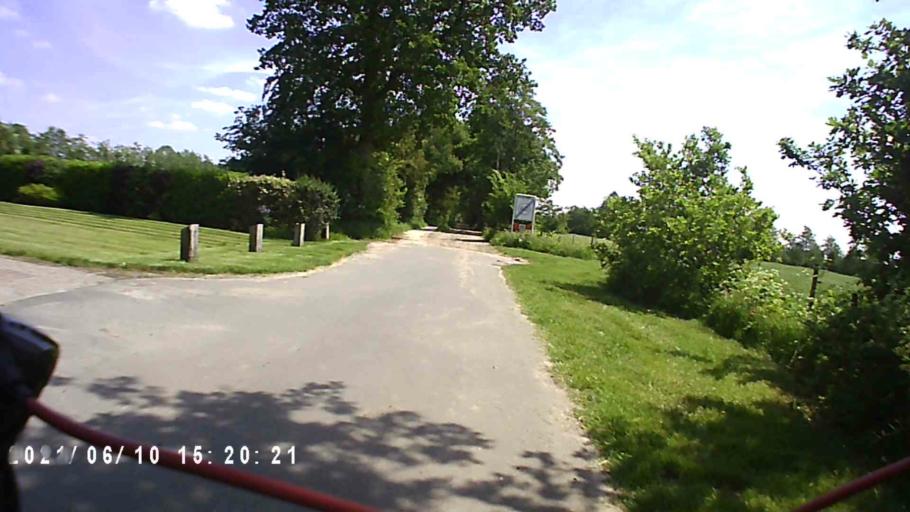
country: NL
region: Friesland
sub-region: Gemeente Achtkarspelen
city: Surhuisterveen
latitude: 53.1923
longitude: 6.1759
